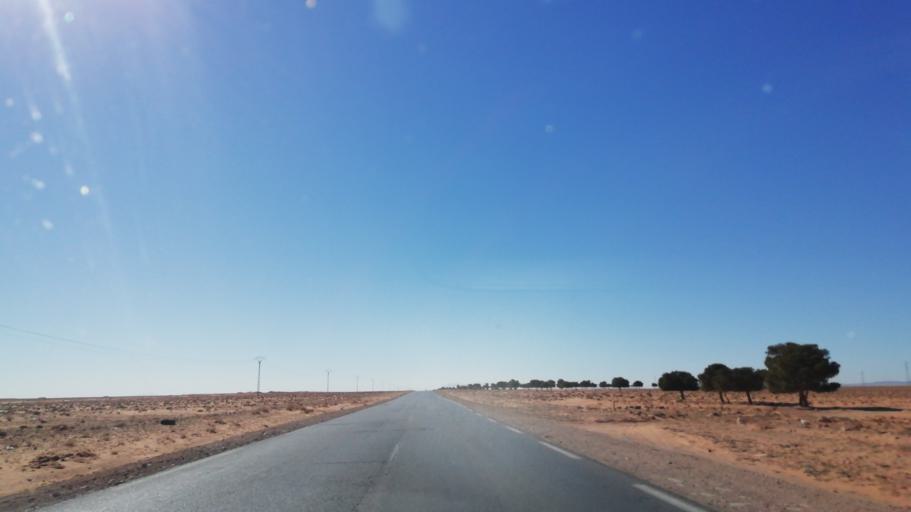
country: DZ
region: Saida
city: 'Ain el Hadjar
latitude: 33.9835
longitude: 0.0304
